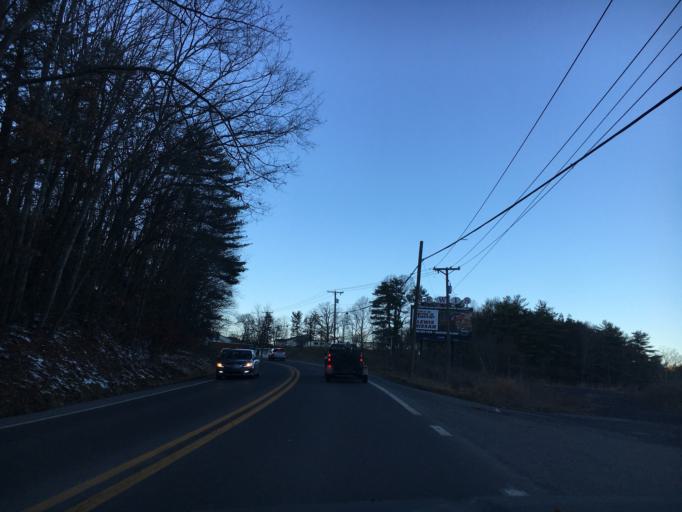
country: US
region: West Virginia
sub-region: Raleigh County
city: Daniels
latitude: 37.7377
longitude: -81.1138
